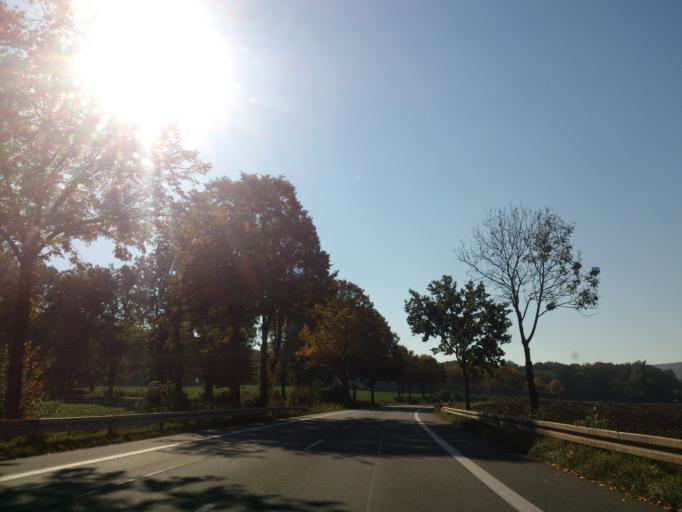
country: DE
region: North Rhine-Westphalia
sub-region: Regierungsbezirk Detmold
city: Willebadessen
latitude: 51.6123
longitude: 9.0359
